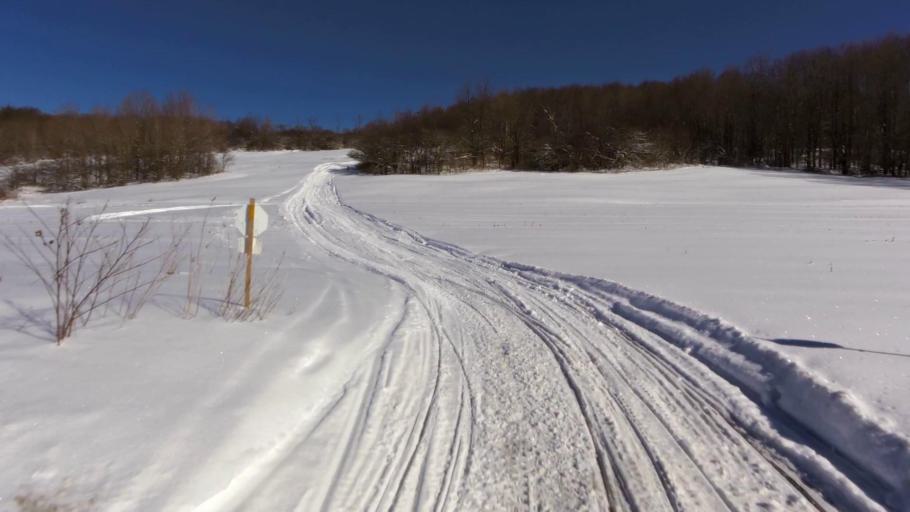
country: US
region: New York
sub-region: Chautauqua County
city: Silver Creek
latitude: 42.3775
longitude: -79.1506
